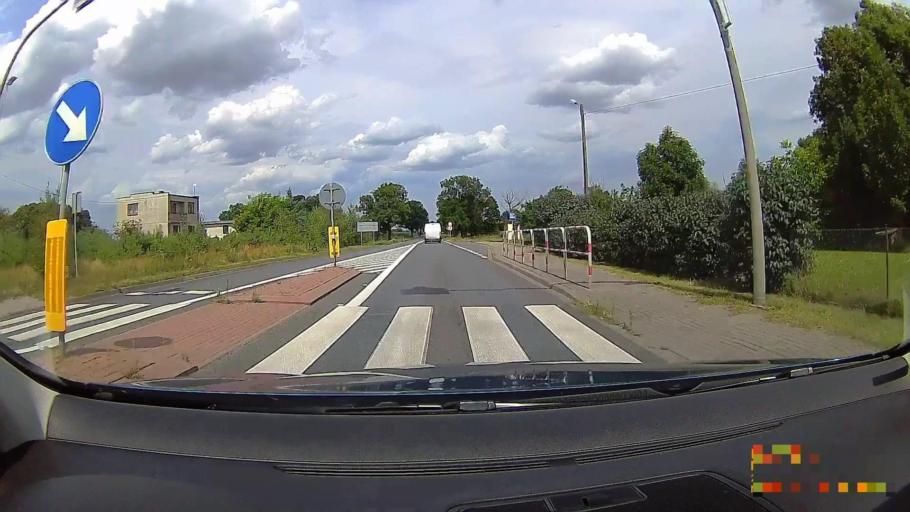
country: PL
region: Greater Poland Voivodeship
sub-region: Powiat koninski
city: Rychwal
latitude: 52.0956
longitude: 18.1666
